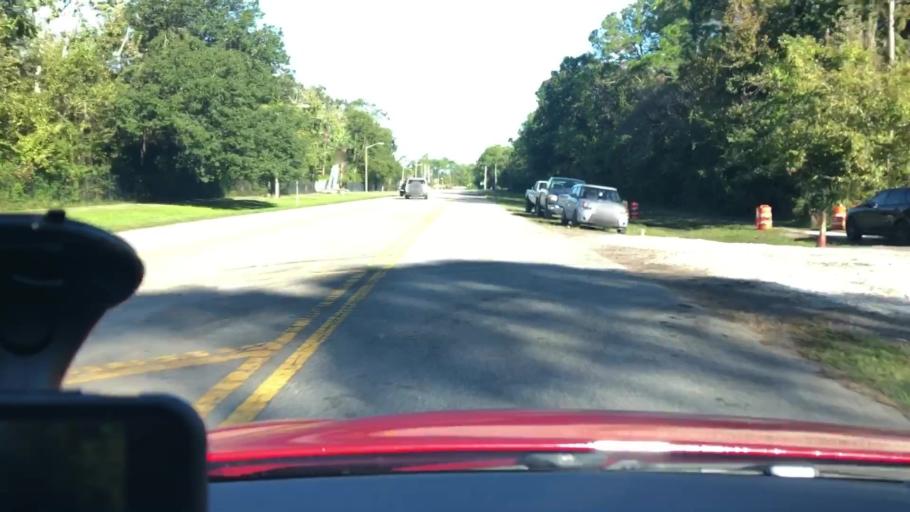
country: US
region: Florida
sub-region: Volusia County
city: Daytona Beach
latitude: 29.2079
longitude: -81.0677
